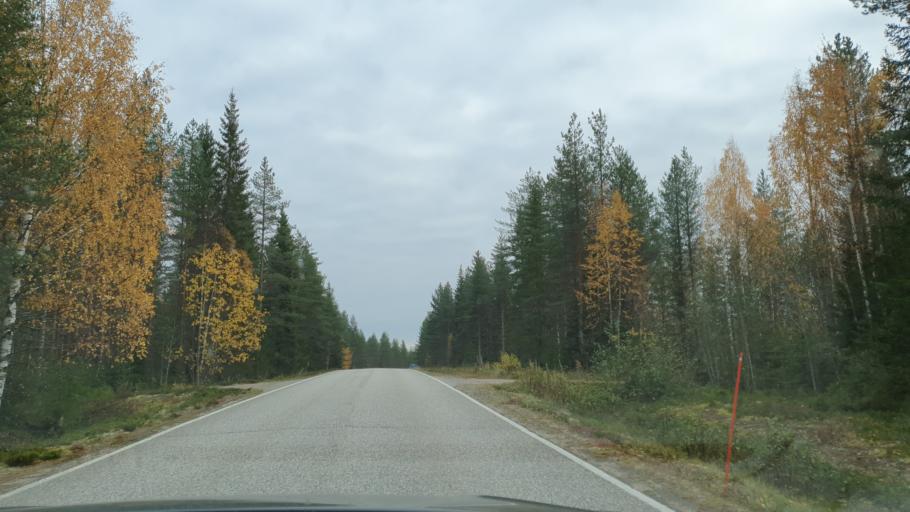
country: FI
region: Kainuu
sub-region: Kajaani
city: Ristijaervi
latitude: 64.4639
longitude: 28.3114
